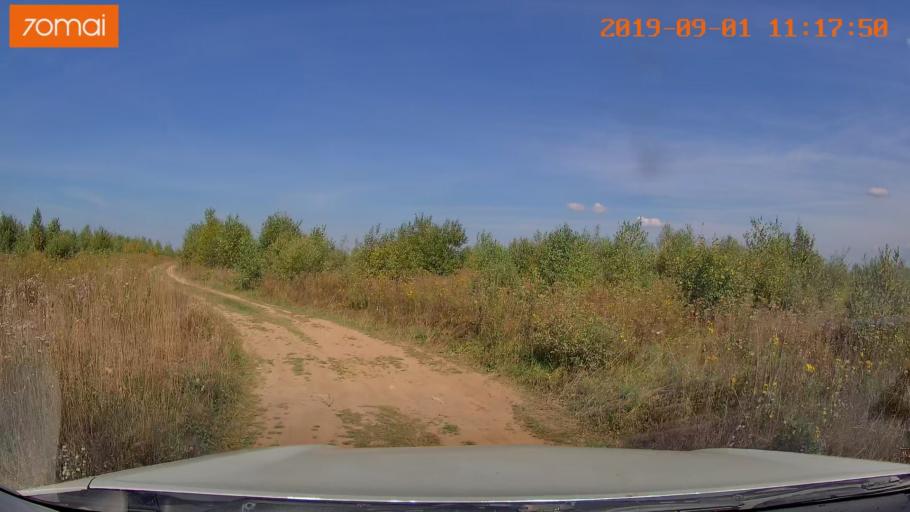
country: RU
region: Kaluga
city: Detchino
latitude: 54.8254
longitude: 36.3663
